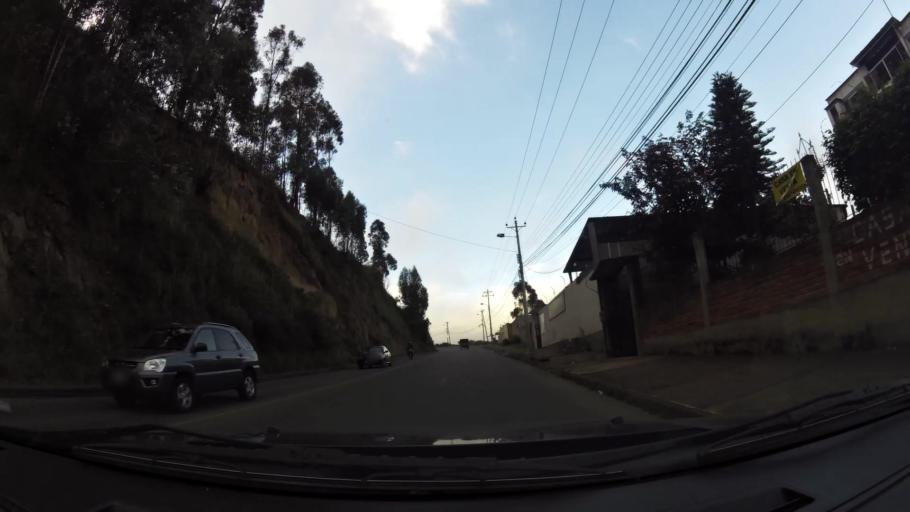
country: EC
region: Pichincha
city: Quito
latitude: -0.2750
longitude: -78.4962
